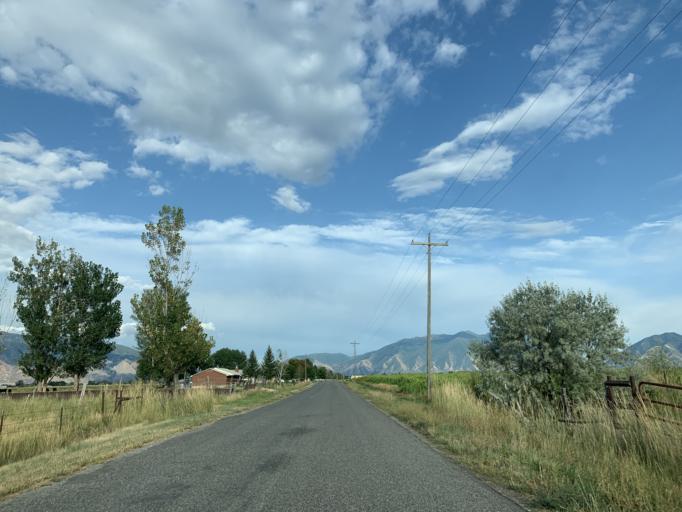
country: US
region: Utah
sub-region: Utah County
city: Benjamin
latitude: 40.1289
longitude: -111.7577
